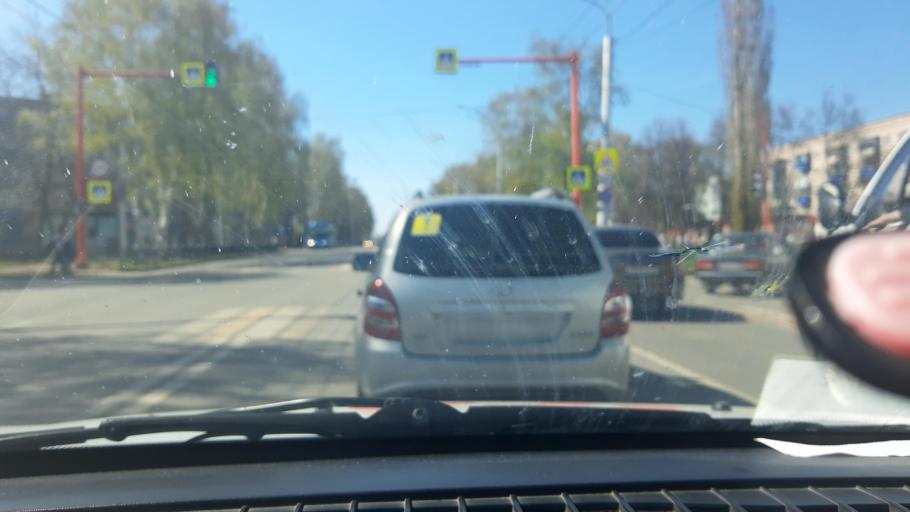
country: RU
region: Bashkortostan
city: Sterlitamak
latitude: 53.6335
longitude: 55.9222
